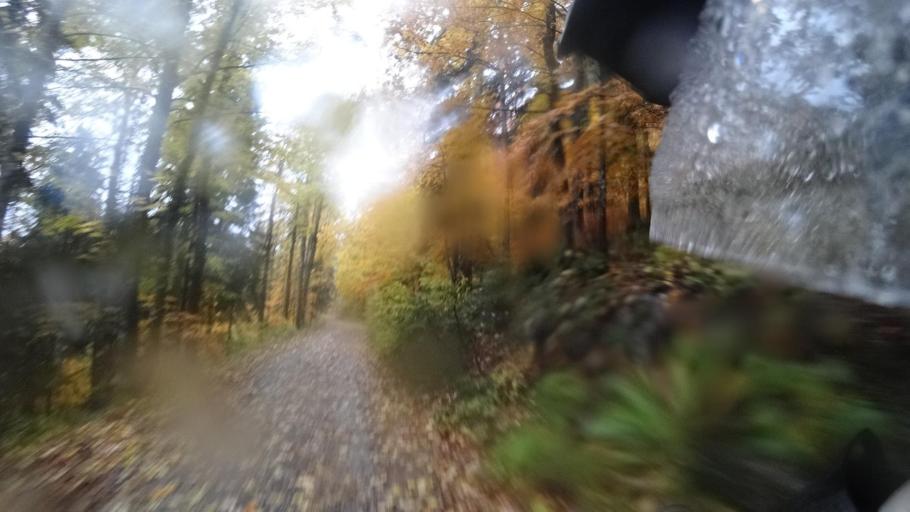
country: HR
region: Primorsko-Goranska
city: Vrbovsko
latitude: 45.3091
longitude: 15.0751
